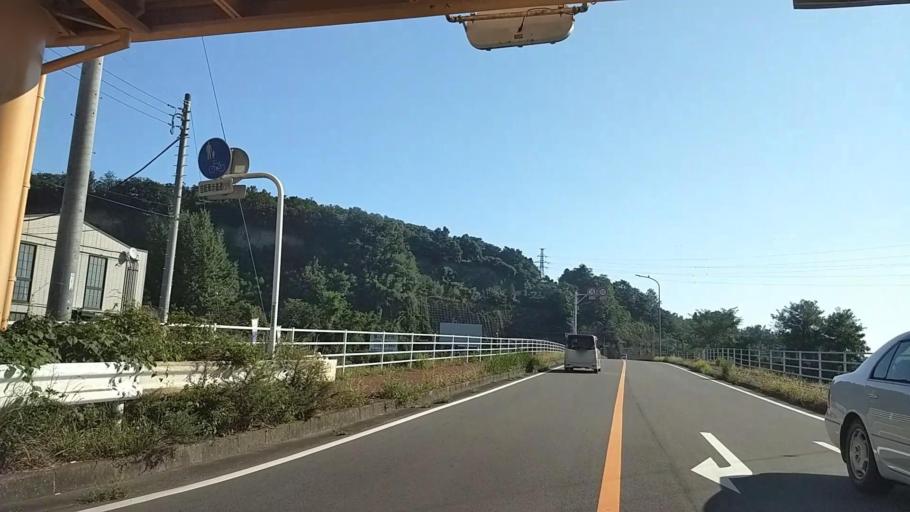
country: JP
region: Gunma
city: Annaka
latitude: 36.3358
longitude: 138.9207
